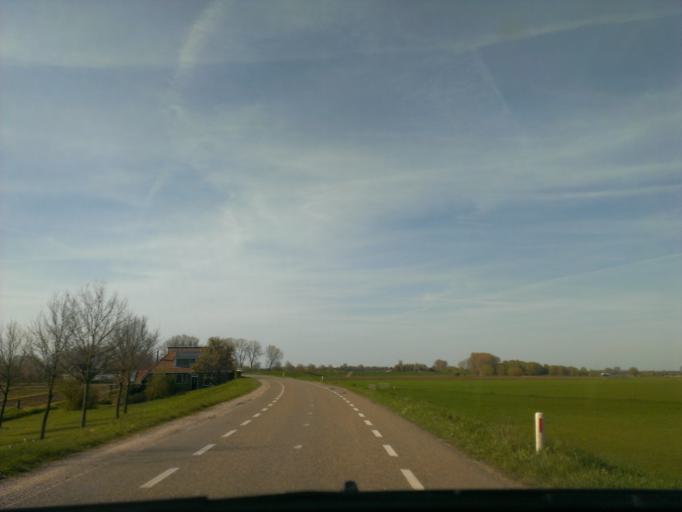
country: NL
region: Overijssel
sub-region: Gemeente Olst-Wijhe
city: Olst
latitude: 52.3129
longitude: 6.0897
